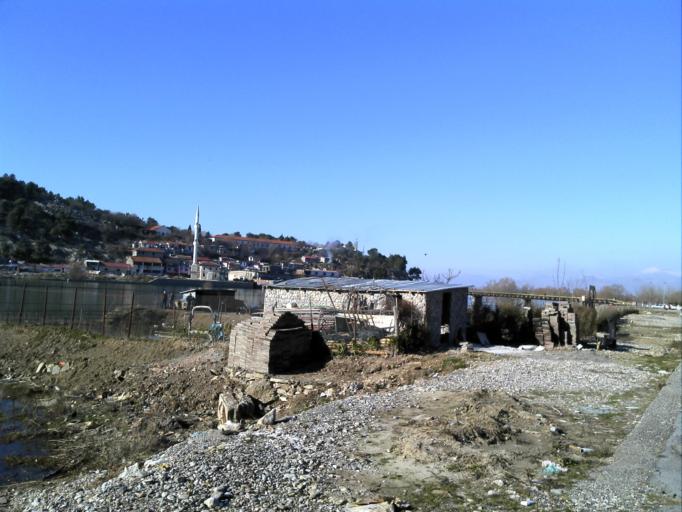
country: AL
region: Shkoder
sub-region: Rrethi i Shkodres
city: Shkoder
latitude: 42.0486
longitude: 19.4921
